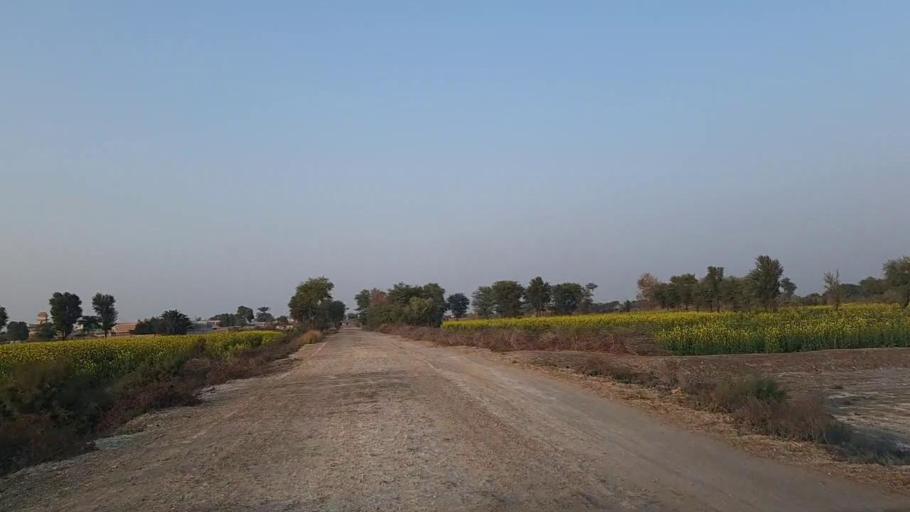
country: PK
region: Sindh
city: Daur
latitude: 26.4323
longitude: 68.3873
